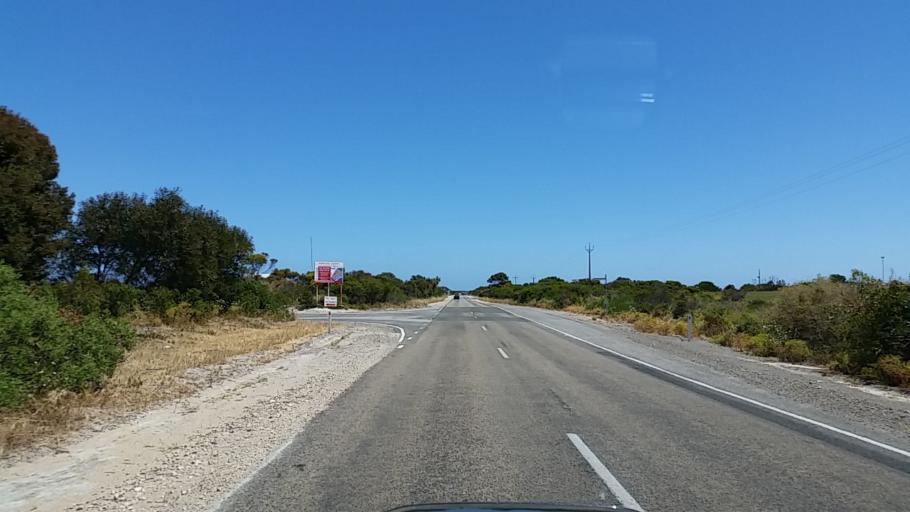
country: AU
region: South Australia
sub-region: Yorke Peninsula
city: Honiton
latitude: -35.2313
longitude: 136.9834
